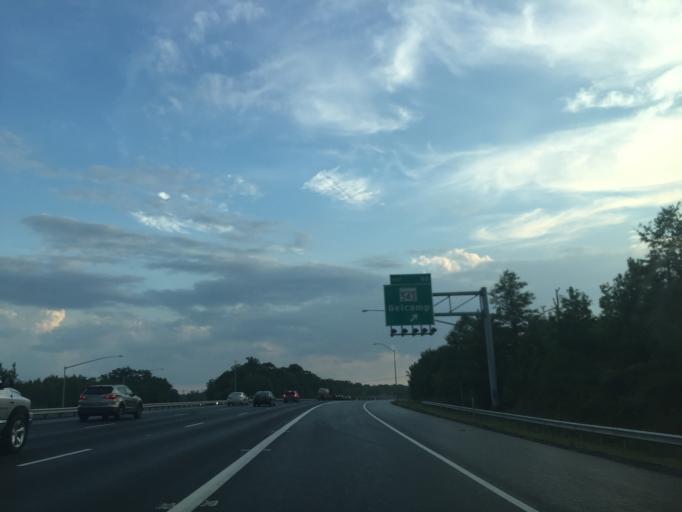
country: US
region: Maryland
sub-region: Harford County
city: Riverside
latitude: 39.4870
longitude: -76.2454
